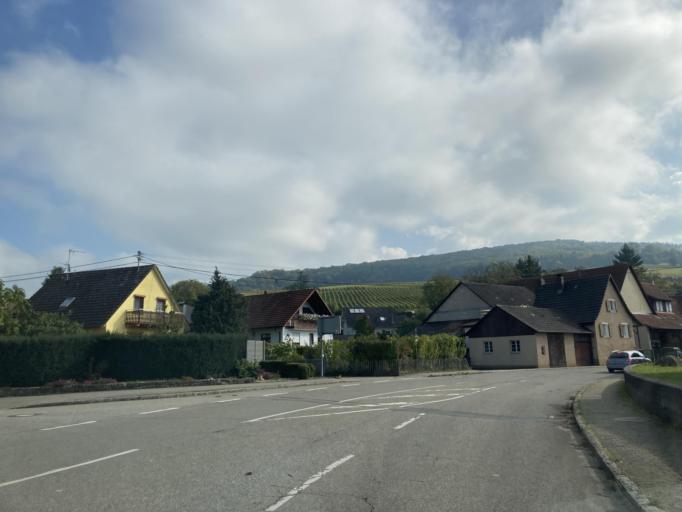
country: DE
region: Baden-Wuerttemberg
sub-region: Freiburg Region
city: Mullheim
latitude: 47.8216
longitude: 7.6522
